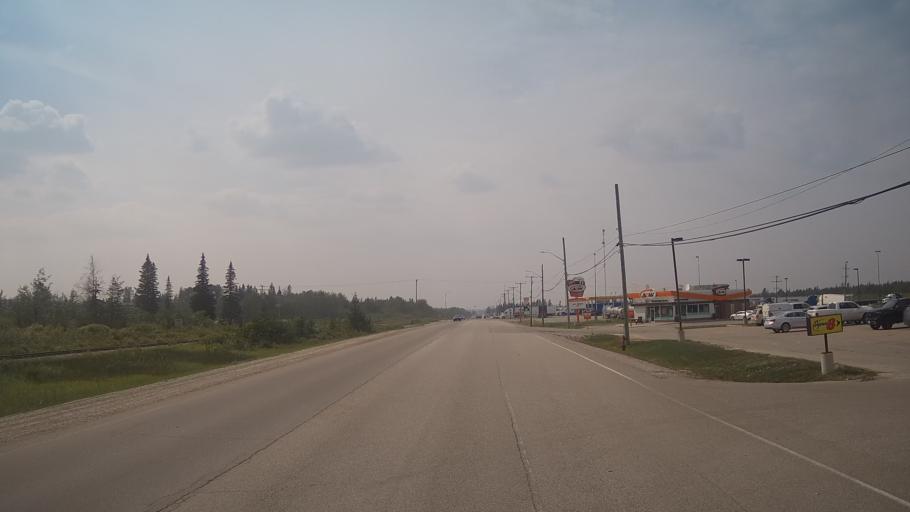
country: CA
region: Ontario
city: Kapuskasing
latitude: 49.3958
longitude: -82.3666
